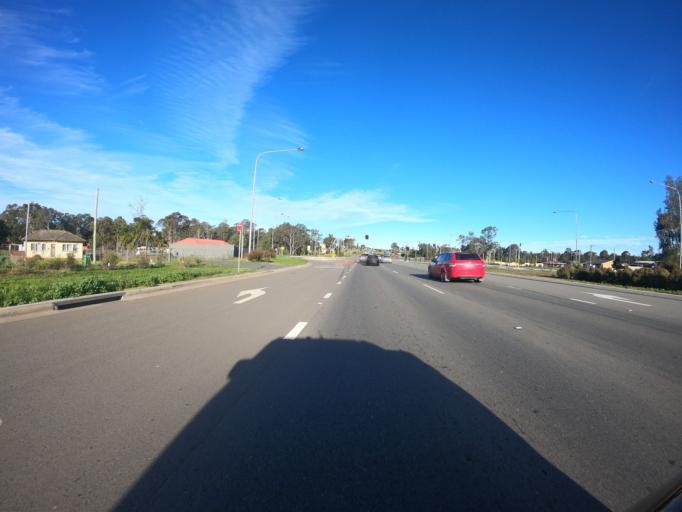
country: AU
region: New South Wales
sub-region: Blacktown
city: Hassall Grove
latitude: -33.6999
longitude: 150.8339
